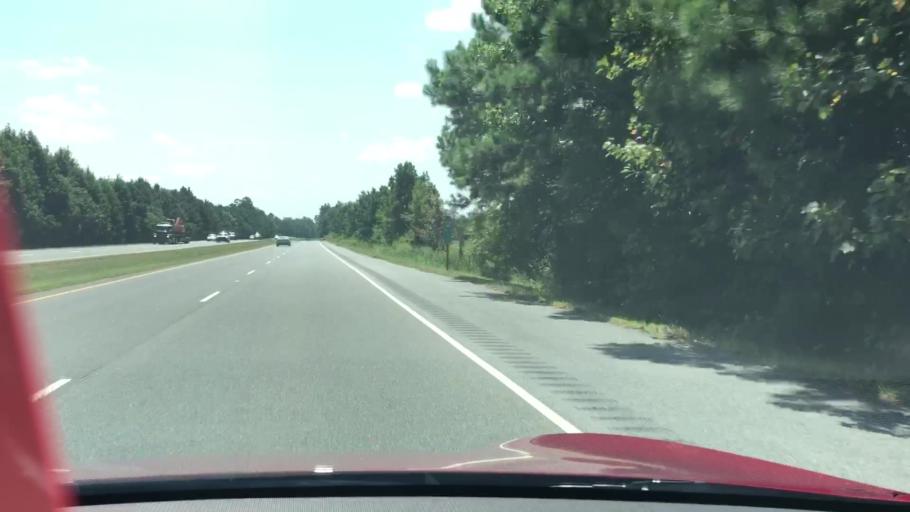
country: US
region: North Carolina
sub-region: Currituck County
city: Moyock
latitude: 36.5904
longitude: -76.1992
